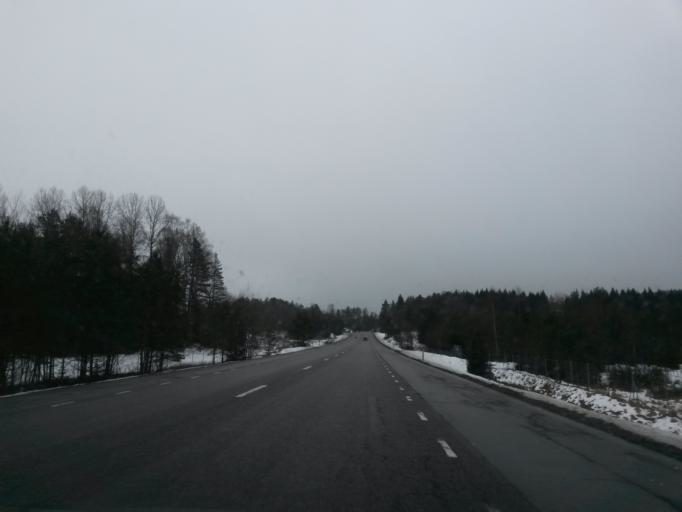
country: SE
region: Vaestra Goetaland
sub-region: Boras Kommun
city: Viskafors
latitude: 57.5990
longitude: 12.8709
